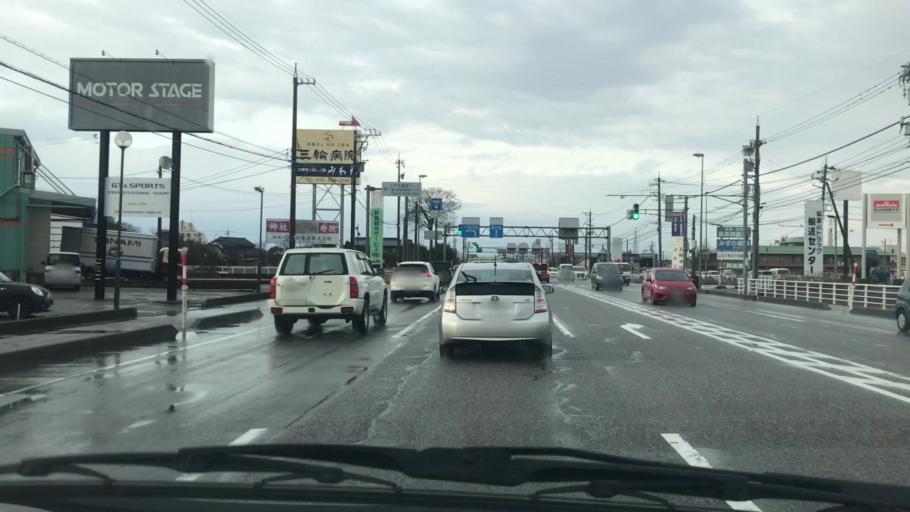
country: JP
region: Toyama
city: Toyama-shi
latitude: 36.6418
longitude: 137.2094
